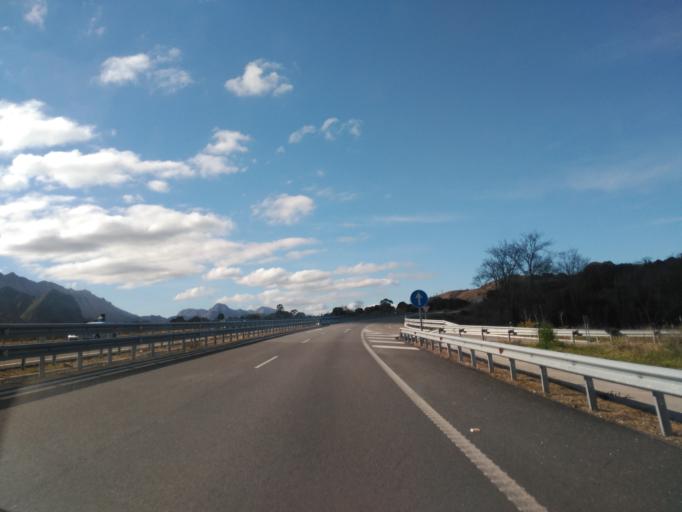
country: ES
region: Asturias
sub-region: Province of Asturias
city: Llanes
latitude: 43.3986
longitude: -4.7148
